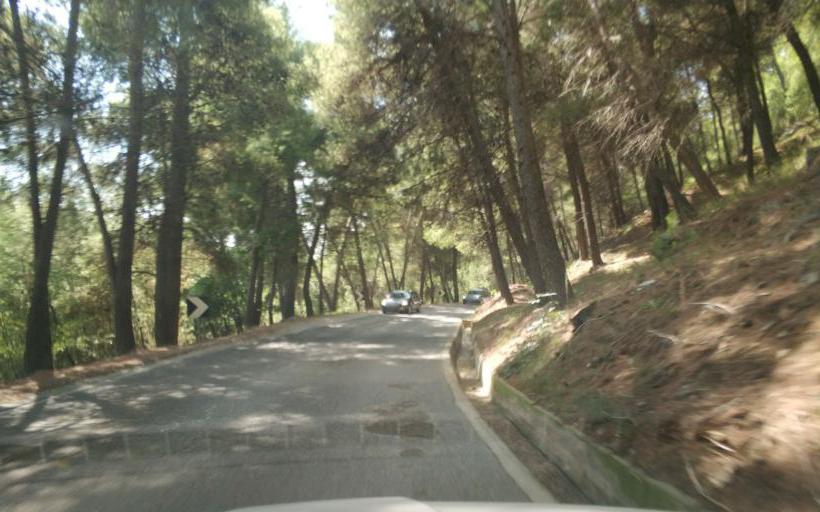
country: AL
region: Durres
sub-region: Rrethi i Krujes
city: Kruje
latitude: 41.4961
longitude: 19.7752
